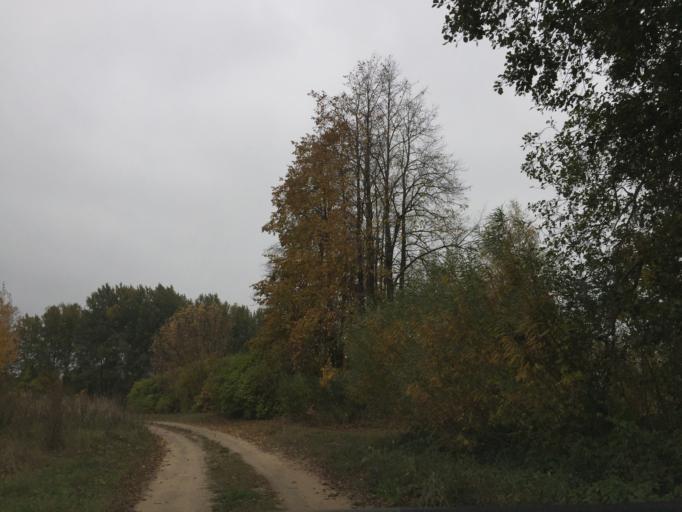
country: LV
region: Dobeles Rajons
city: Dobele
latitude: 56.6780
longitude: 23.4481
